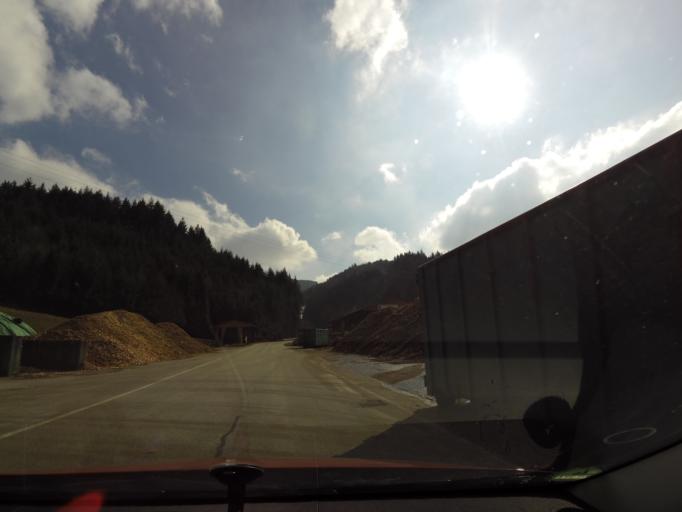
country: DE
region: Baden-Wuerttemberg
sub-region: Freiburg Region
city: Ottenhofen im Schwarzwald
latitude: 48.5540
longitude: 8.1565
